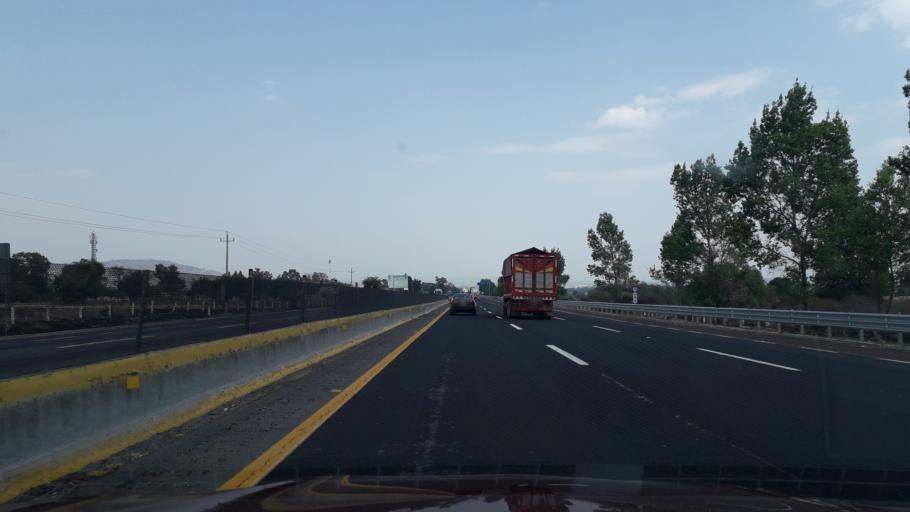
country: MX
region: Puebla
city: San Matias Tlalancaleca
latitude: 19.3229
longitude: -98.5205
